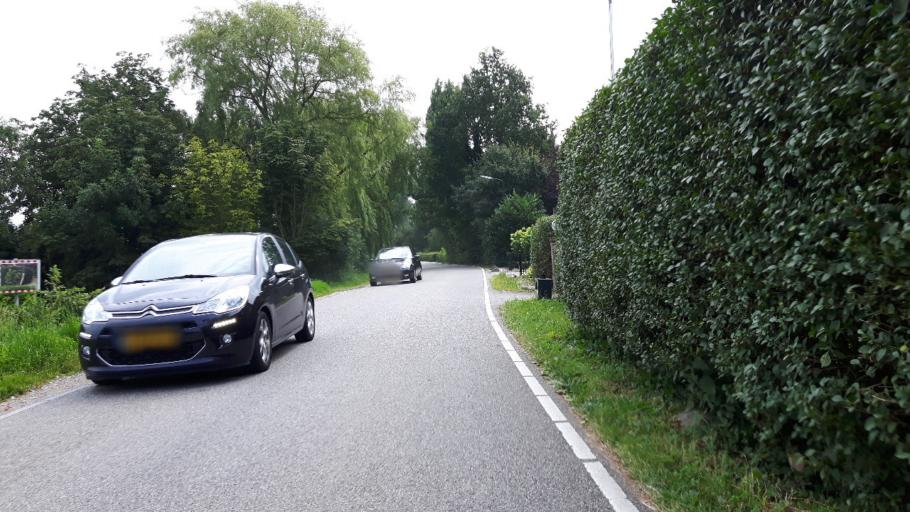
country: NL
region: Utrecht
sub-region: Gemeente IJsselstein
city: IJsselstein
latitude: 52.0461
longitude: 5.0219
